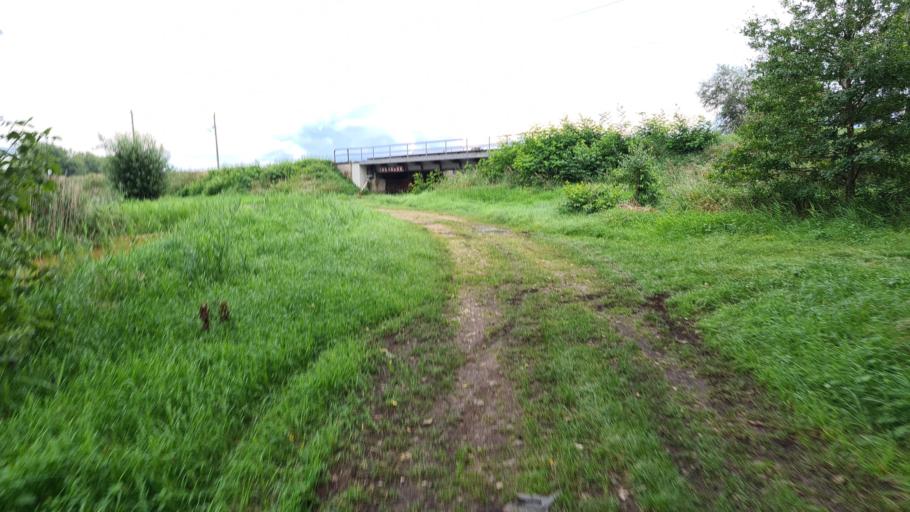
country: DE
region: Brandenburg
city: Bad Liebenwerda
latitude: 51.5267
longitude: 13.3690
